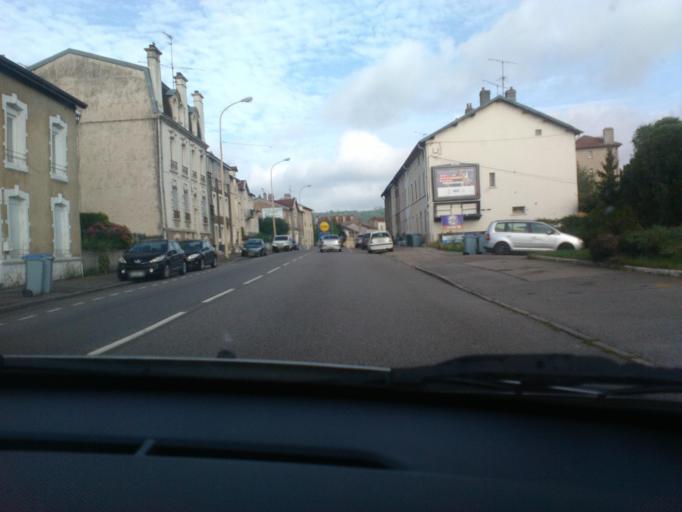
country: FR
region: Lorraine
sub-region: Departement de Meurthe-et-Moselle
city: Frouard
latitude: 48.7583
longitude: 6.1357
